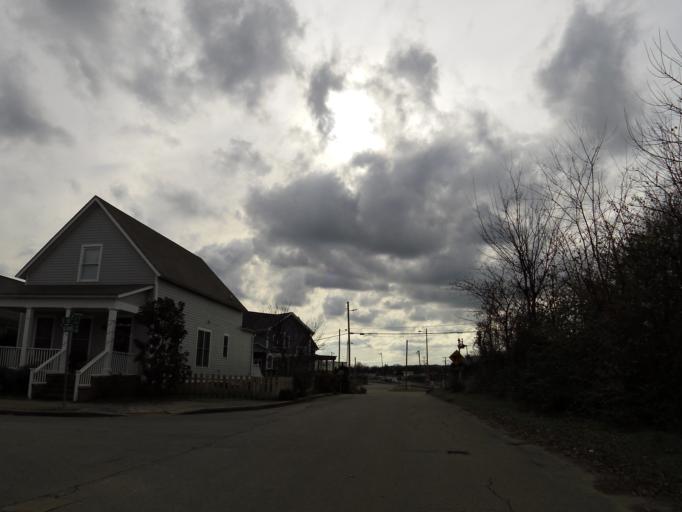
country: US
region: Tennessee
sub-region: Hamilton County
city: Chattanooga
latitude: 35.0315
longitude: -85.3025
